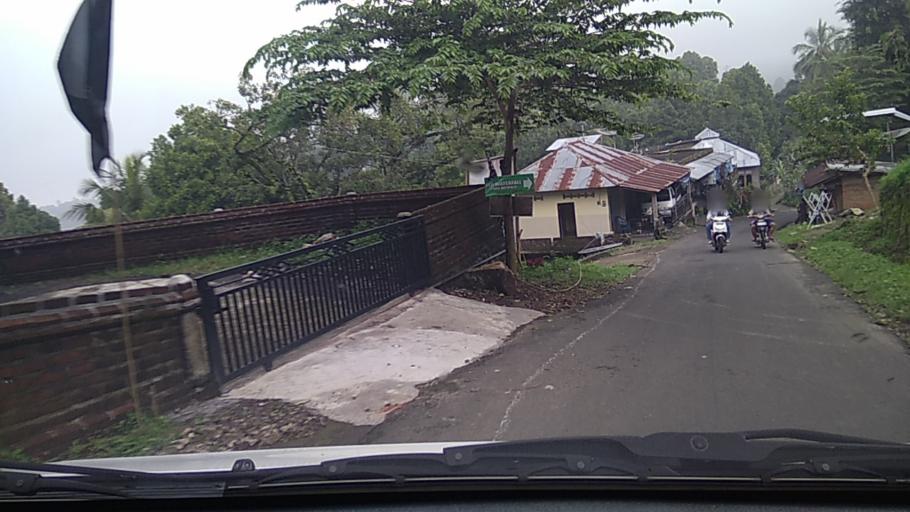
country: ID
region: Bali
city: Banjar Padangbulia
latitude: -8.1862
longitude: 115.1868
